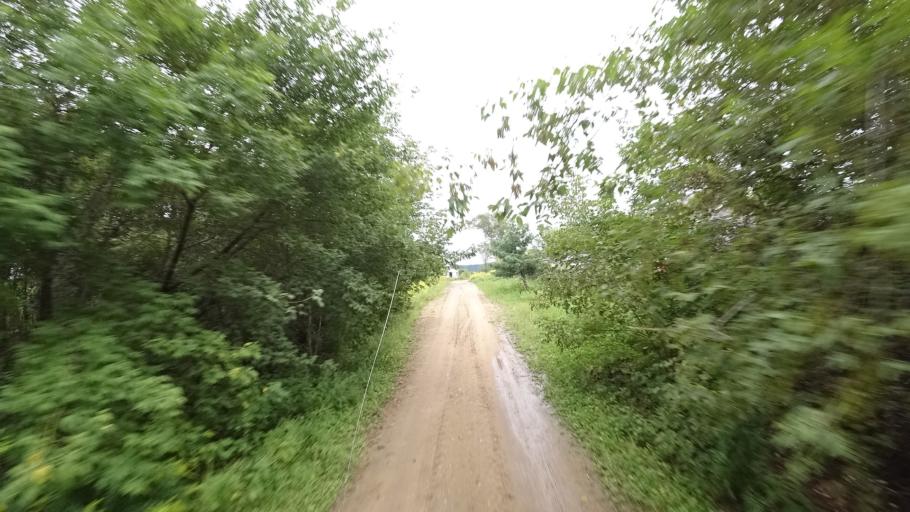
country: RU
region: Primorskiy
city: Rettikhovka
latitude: 44.1591
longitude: 132.7444
